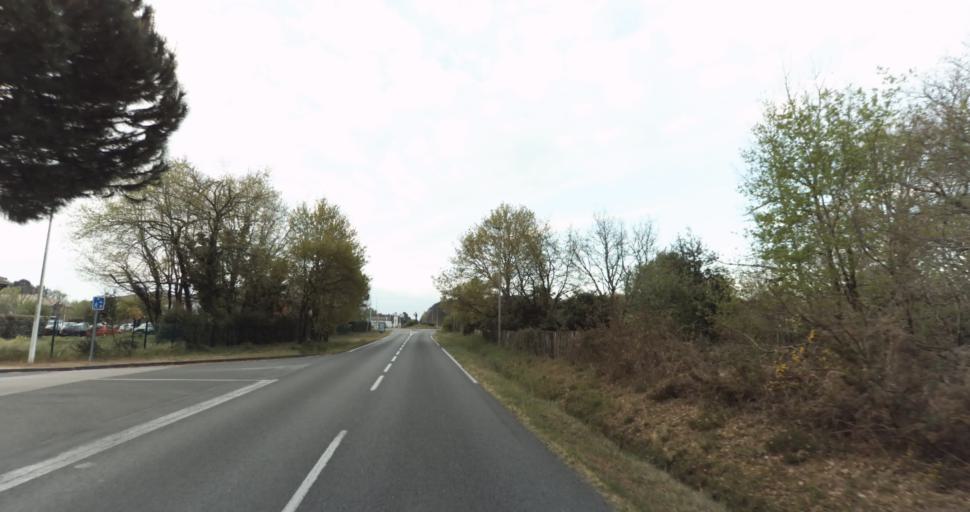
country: FR
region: Aquitaine
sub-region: Departement de la Gironde
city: Martignas-sur-Jalle
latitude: 44.8019
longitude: -0.7783
